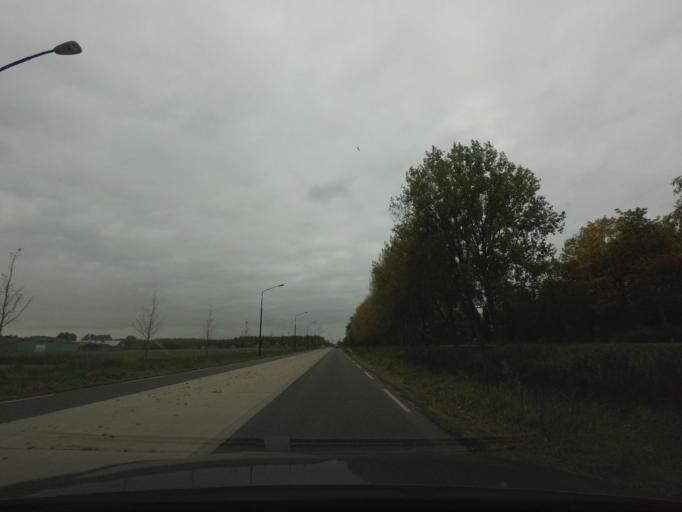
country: NL
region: North Holland
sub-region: Gemeente Heerhugowaard
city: Heerhugowaard
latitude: 52.6671
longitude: 4.8584
